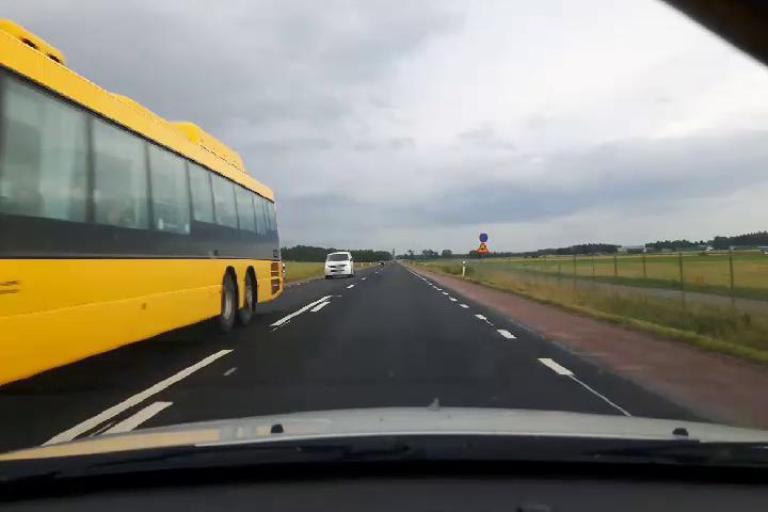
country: SE
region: Uppsala
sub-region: Uppsala Kommun
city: Gamla Uppsala
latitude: 59.8968
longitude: 17.6140
